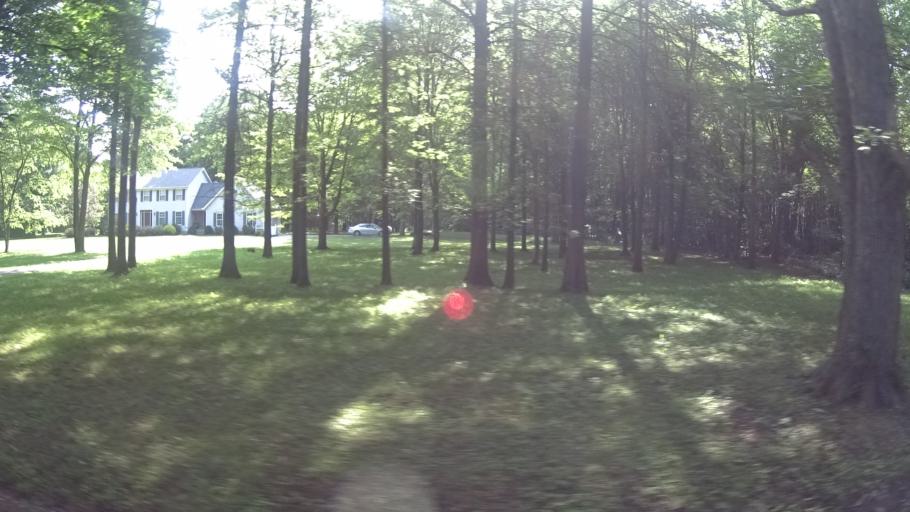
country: US
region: Ohio
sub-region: Lorain County
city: Vermilion
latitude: 41.3688
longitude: -82.4304
